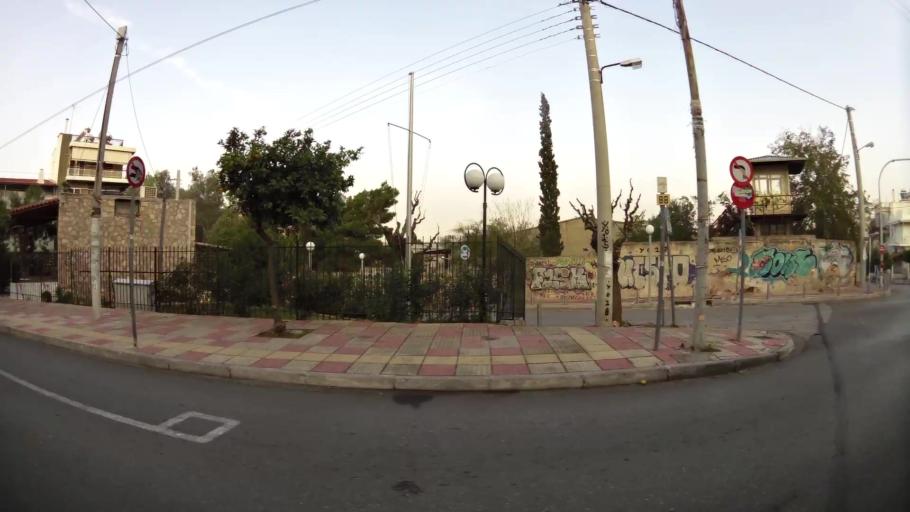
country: GR
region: Attica
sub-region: Nomarchia Athinas
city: Ymittos
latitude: 37.9508
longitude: 23.7461
